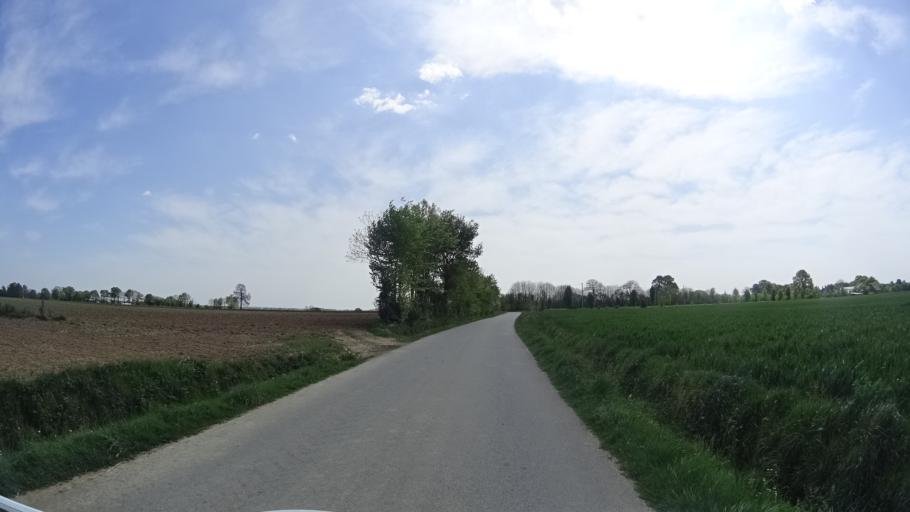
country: FR
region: Brittany
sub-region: Departement d'Ille-et-Vilaine
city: Torce
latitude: 48.0400
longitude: -1.2820
